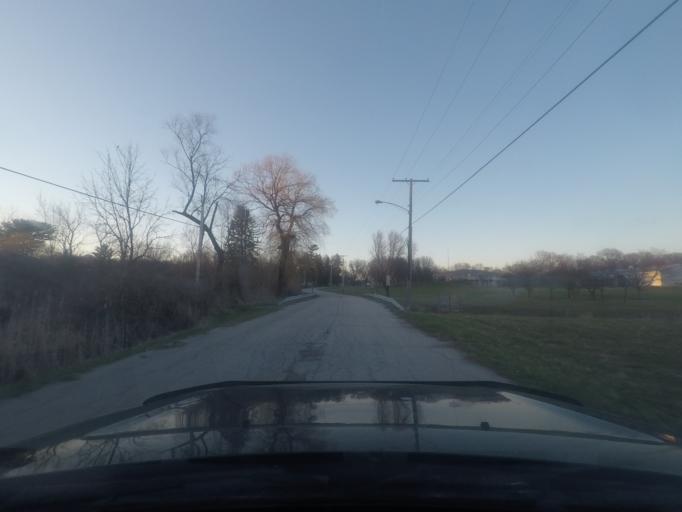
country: US
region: Indiana
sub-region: LaPorte County
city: Kingsford Heights
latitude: 41.5192
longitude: -86.7019
